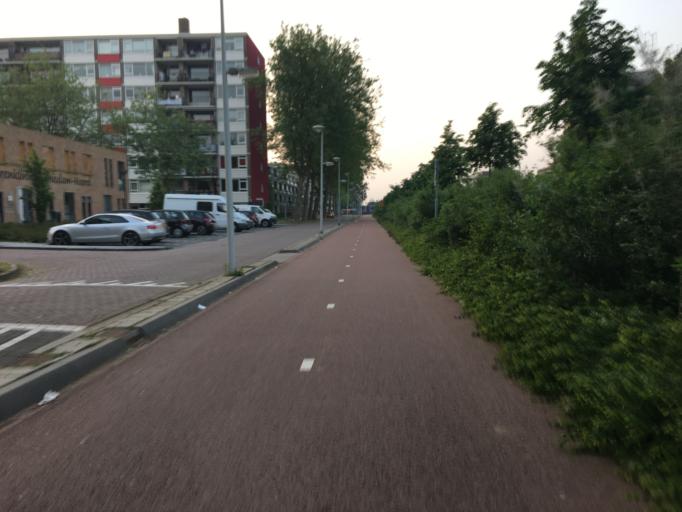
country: NL
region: South Holland
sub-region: Gemeente Schiedam
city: Schiedam
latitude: 51.9312
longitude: 4.3749
